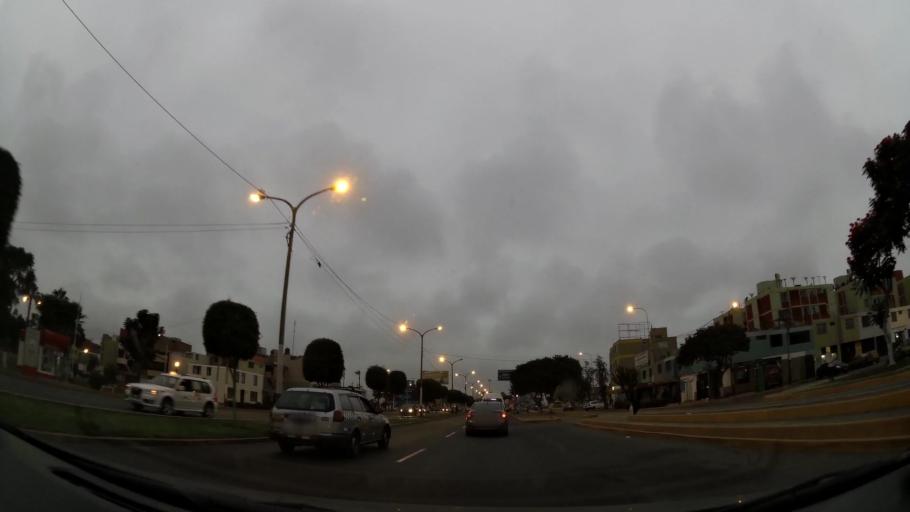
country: PE
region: Callao
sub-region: Callao
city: Callao
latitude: -12.0558
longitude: -77.1091
